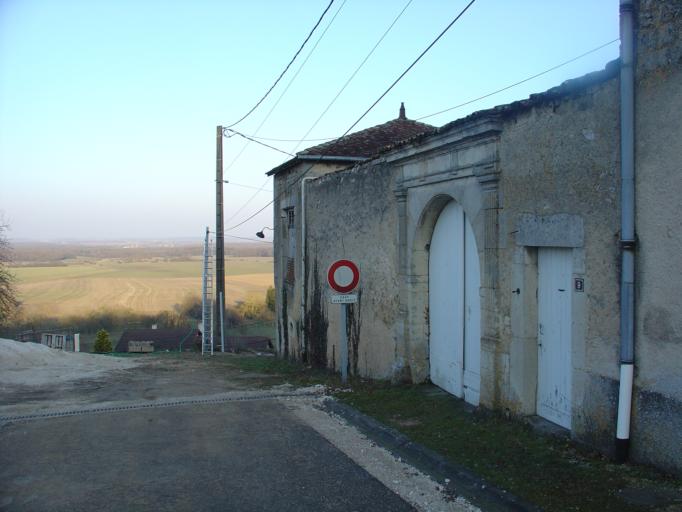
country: FR
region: Lorraine
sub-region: Departement de Meurthe-et-Moselle
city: Foug
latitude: 48.7475
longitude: 5.7629
